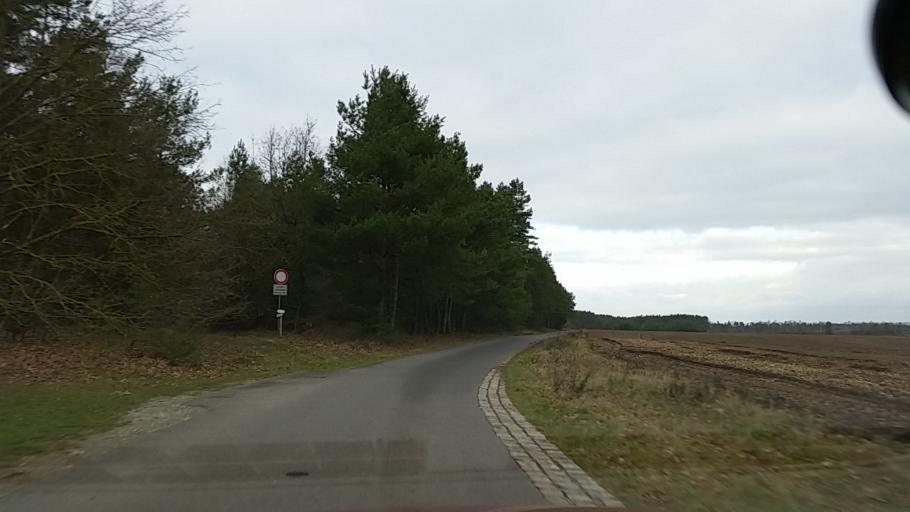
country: DE
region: Lower Saxony
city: Wieren
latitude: 52.8561
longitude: 10.6591
